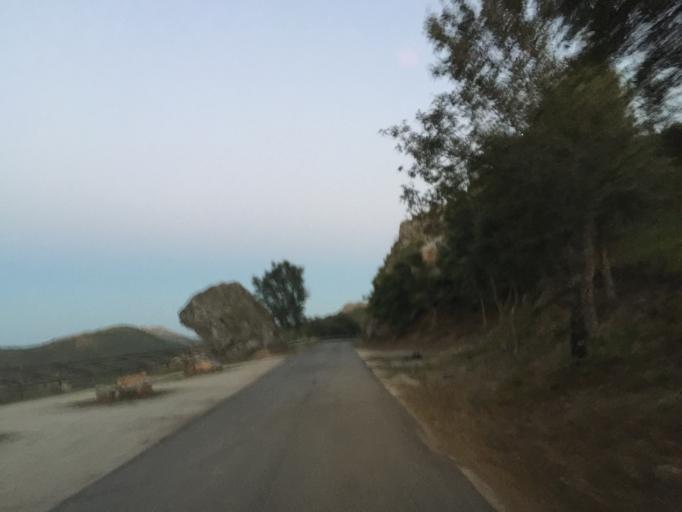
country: PT
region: Portalegre
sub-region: Castelo de Vide
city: Castelo de Vide
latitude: 39.4037
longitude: -7.4554
